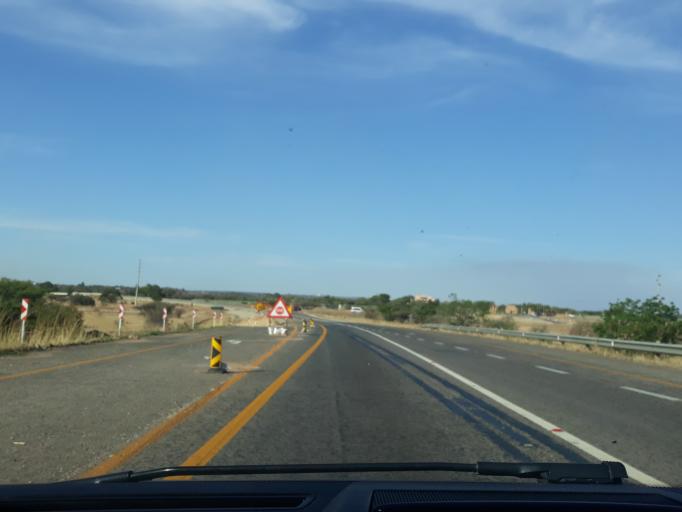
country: ZA
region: Limpopo
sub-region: Capricorn District Municipality
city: Polokwane
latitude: -23.9451
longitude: 29.4163
